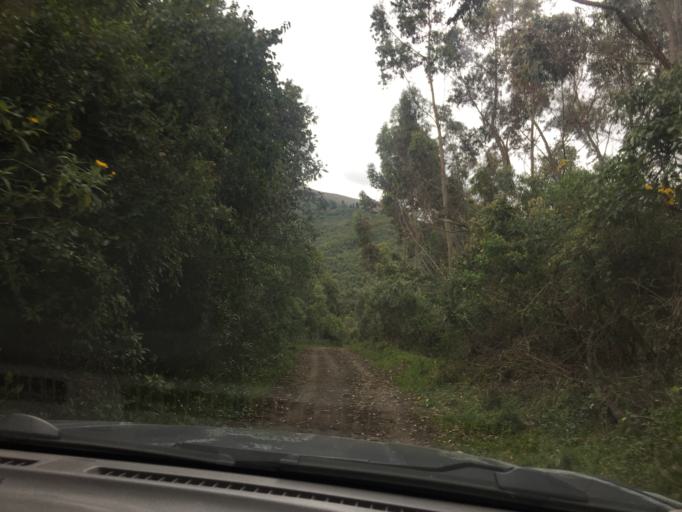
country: EC
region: Pichincha
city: Cayambe
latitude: 0.0745
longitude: -78.2997
